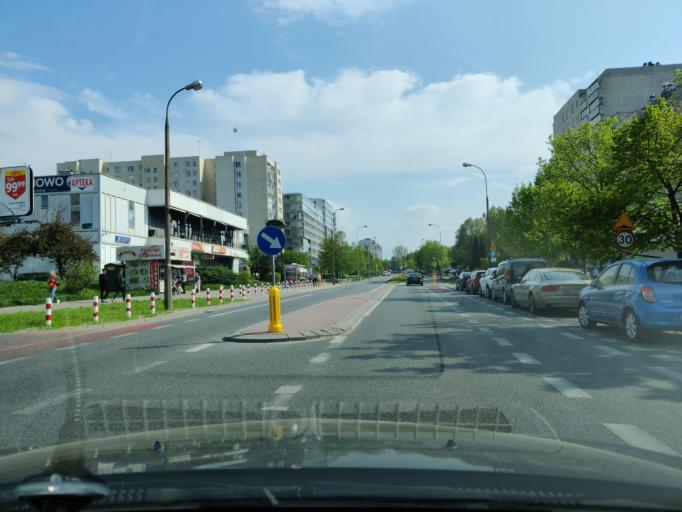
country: PL
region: Masovian Voivodeship
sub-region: Warszawa
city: Ursynow
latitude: 52.1459
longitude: 21.0433
